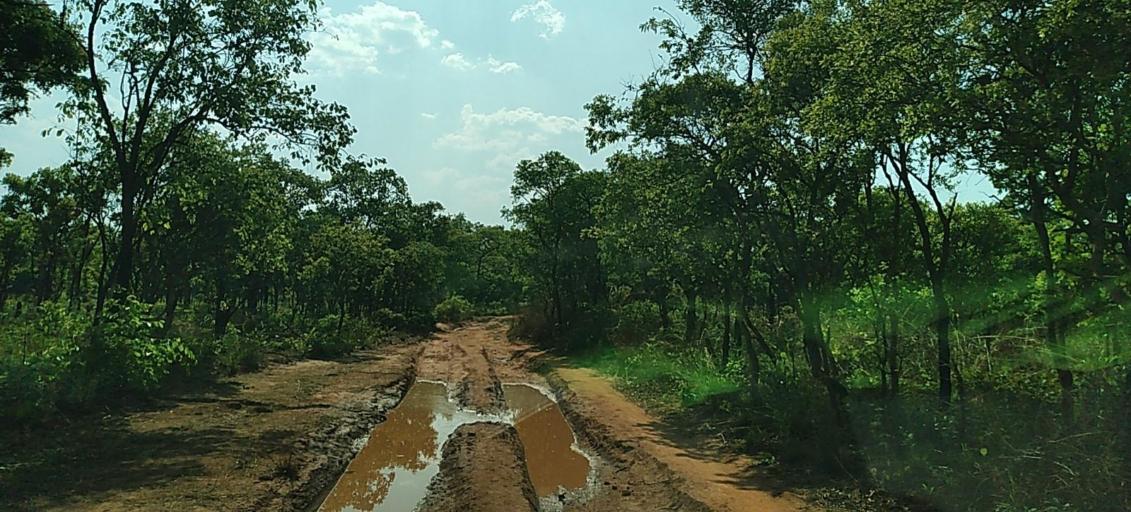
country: ZM
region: North-Western
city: Mwinilunga
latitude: -11.2991
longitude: 24.8675
